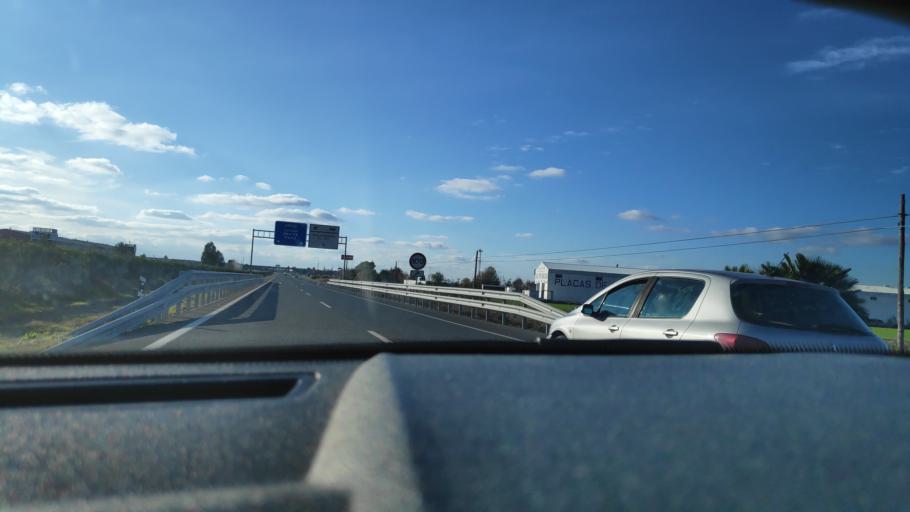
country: ES
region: Andalusia
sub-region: Provincia de Sevilla
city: Ecija
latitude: 37.5229
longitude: -5.1477
